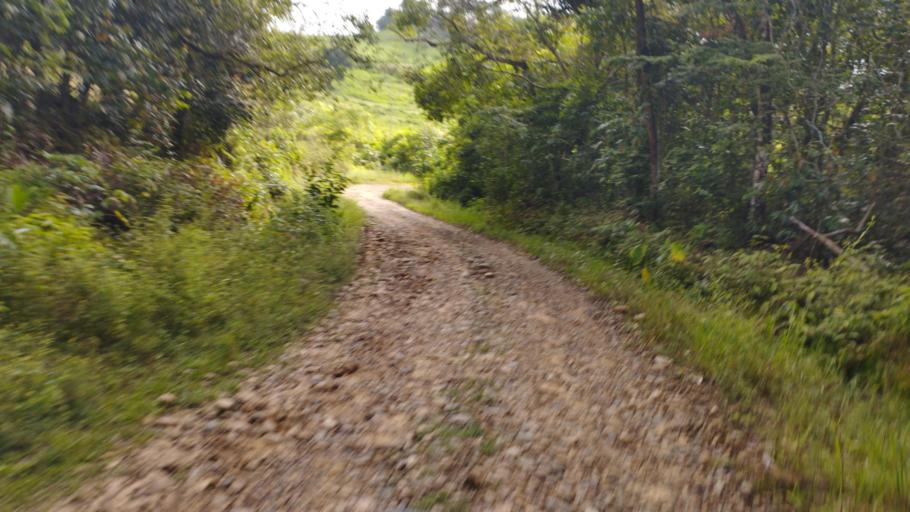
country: CO
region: Casanare
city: Sabanalarga
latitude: 4.7610
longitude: -73.0808
